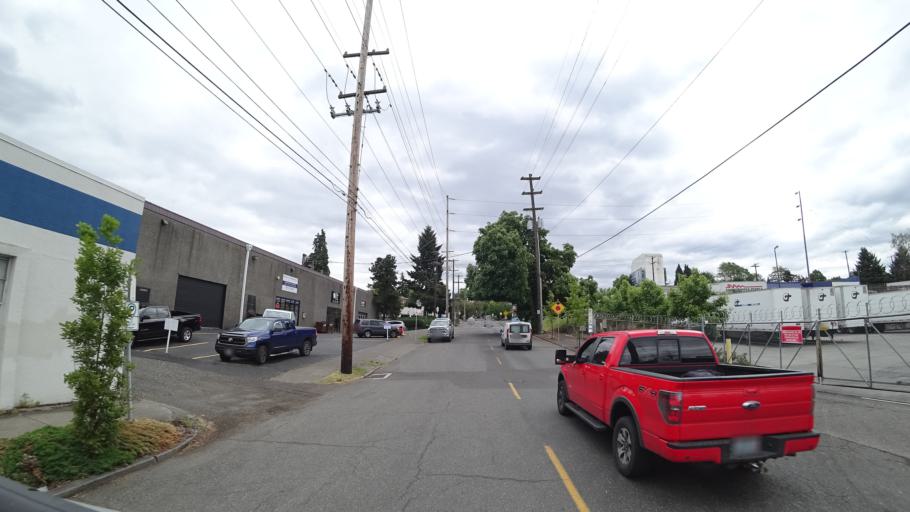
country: US
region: Oregon
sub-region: Multnomah County
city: Portland
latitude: 45.5028
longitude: -122.6578
